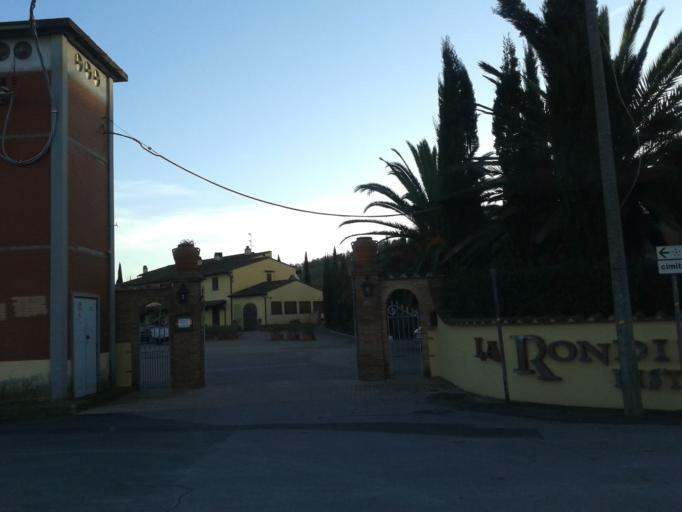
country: IT
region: Tuscany
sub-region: Provincia di Livorno
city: Guasticce
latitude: 43.5952
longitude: 10.4053
